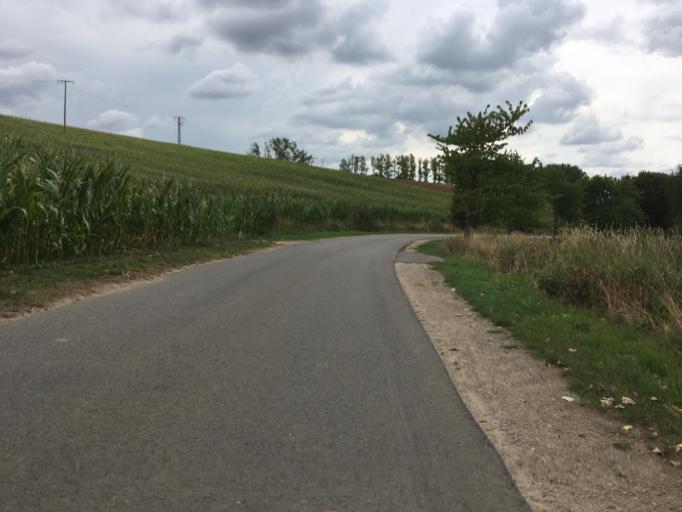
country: DE
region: Brandenburg
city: Prenzlau
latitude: 53.2578
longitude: 13.8841
